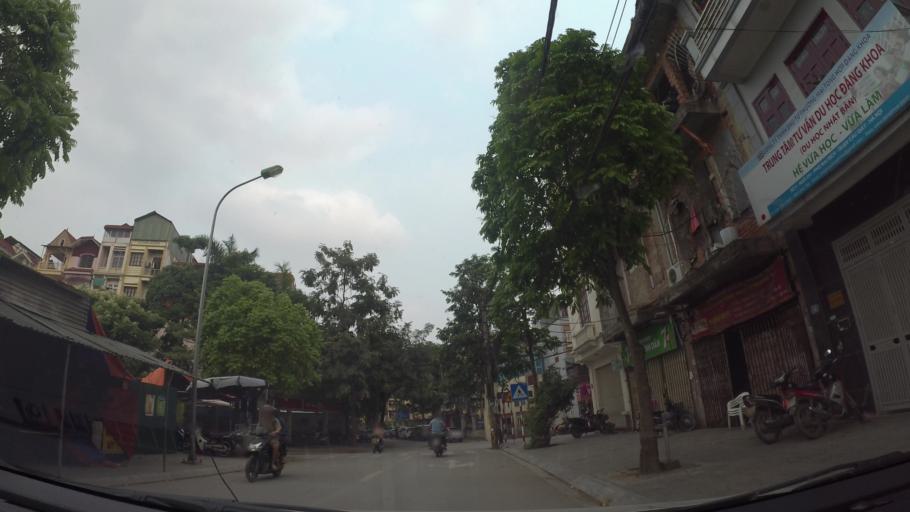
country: VN
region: Ha Noi
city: Cau Dien
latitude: 21.0448
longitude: 105.7753
